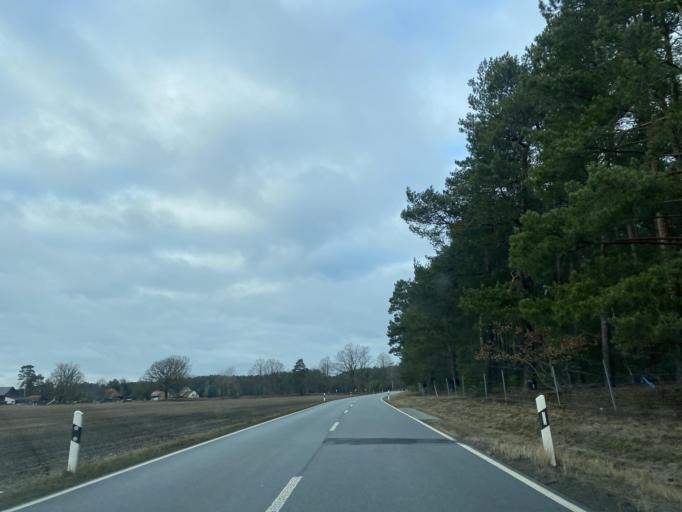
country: PL
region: Lubusz
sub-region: Powiat zarski
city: Leknica
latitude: 51.5104
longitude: 14.7787
